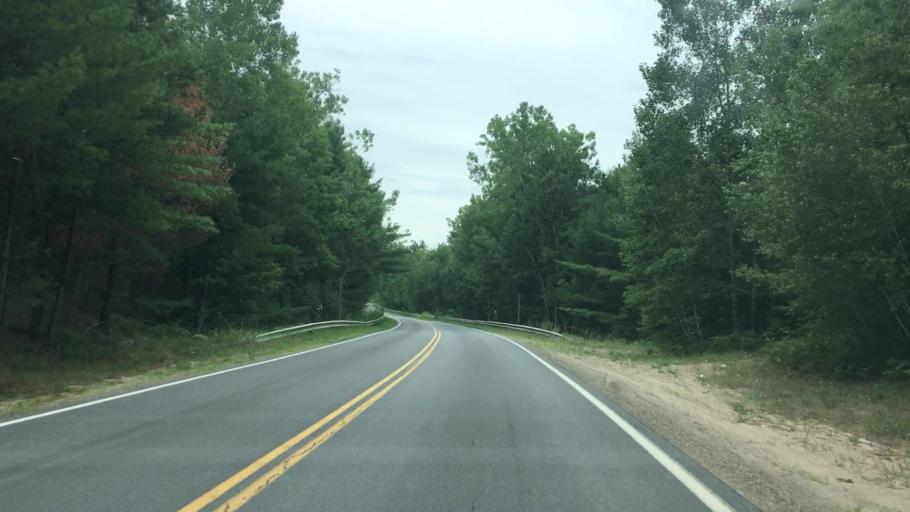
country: US
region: New York
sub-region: Essex County
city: Keeseville
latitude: 44.4745
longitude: -73.5949
